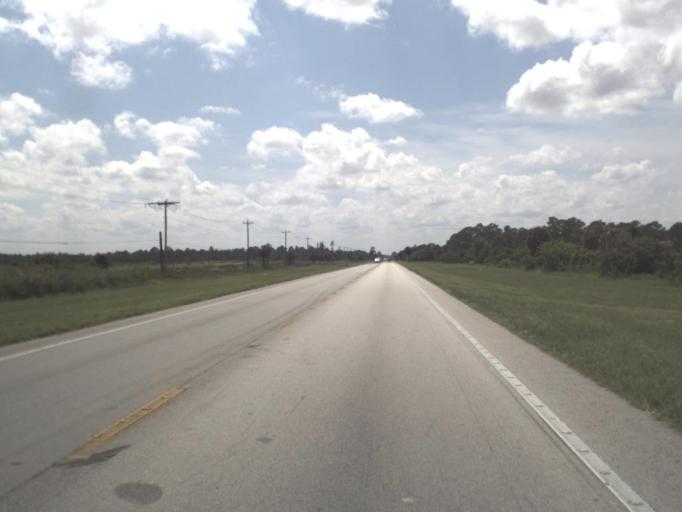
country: US
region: Florida
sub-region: Collier County
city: Immokalee
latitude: 26.4565
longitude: -81.4342
